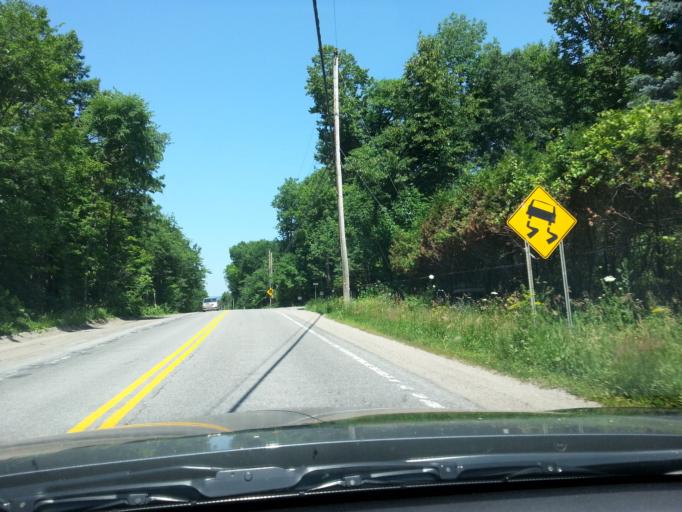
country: CA
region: Ontario
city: Bells Corners
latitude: 45.4688
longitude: -75.9414
